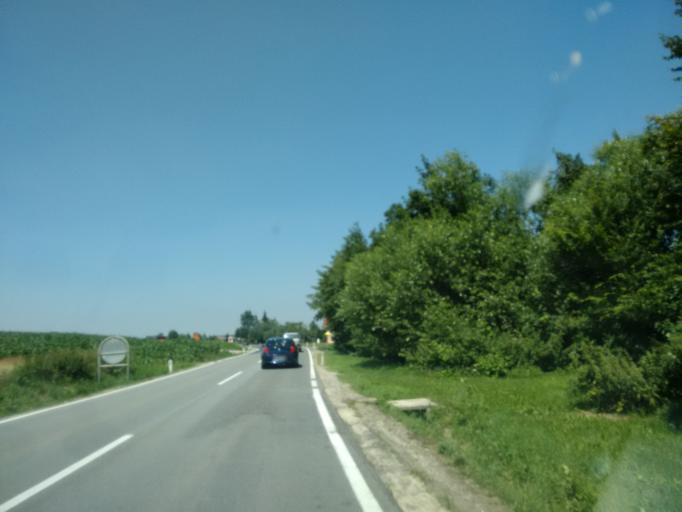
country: AT
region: Upper Austria
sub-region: Politischer Bezirk Grieskirchen
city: Bad Schallerbach
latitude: 48.2300
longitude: 13.9667
